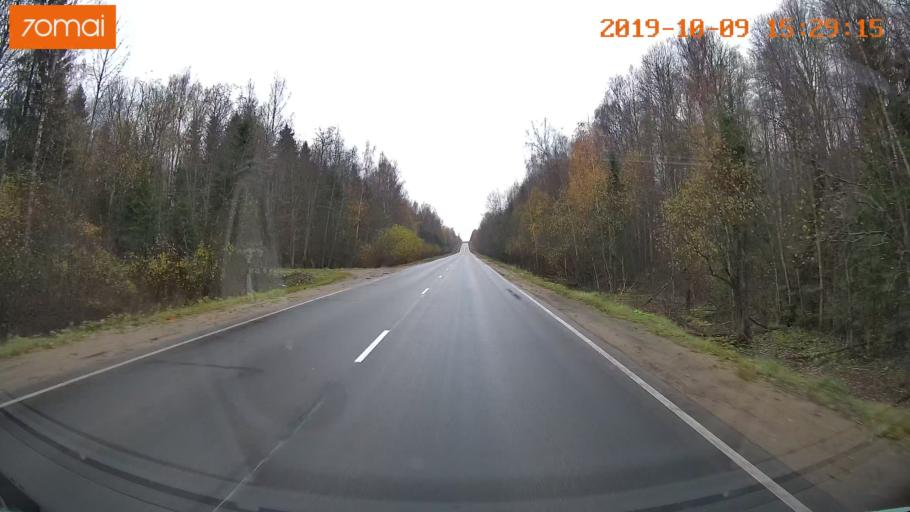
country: RU
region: Kostroma
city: Susanino
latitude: 57.9936
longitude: 41.3459
